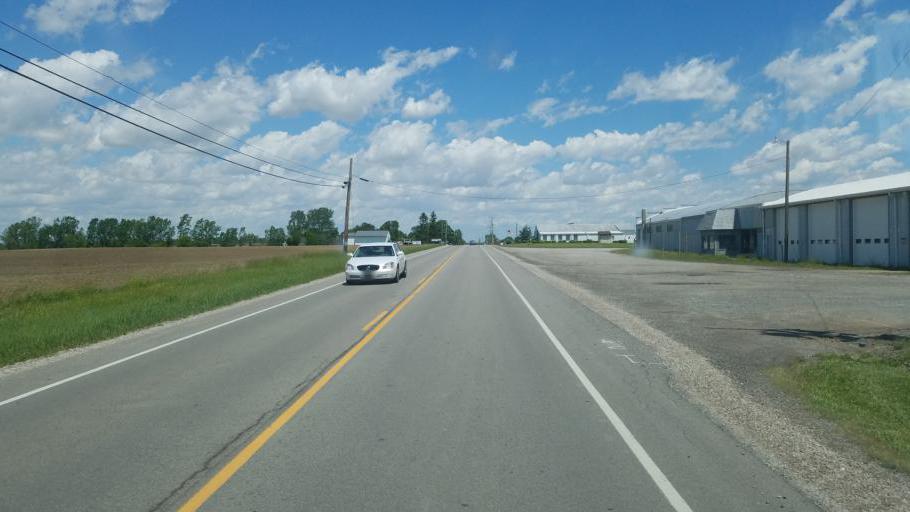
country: US
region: Ohio
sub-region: Huron County
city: Willard
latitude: 41.0380
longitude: -82.7321
